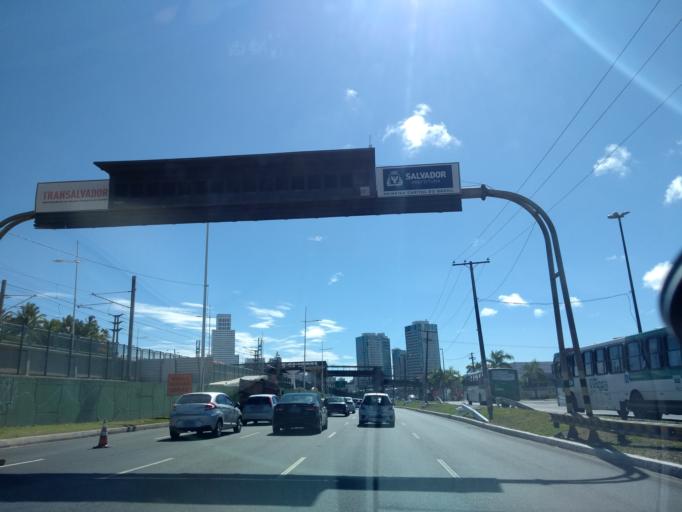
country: BR
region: Bahia
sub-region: Salvador
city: Salvador
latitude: -12.9742
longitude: -38.4512
